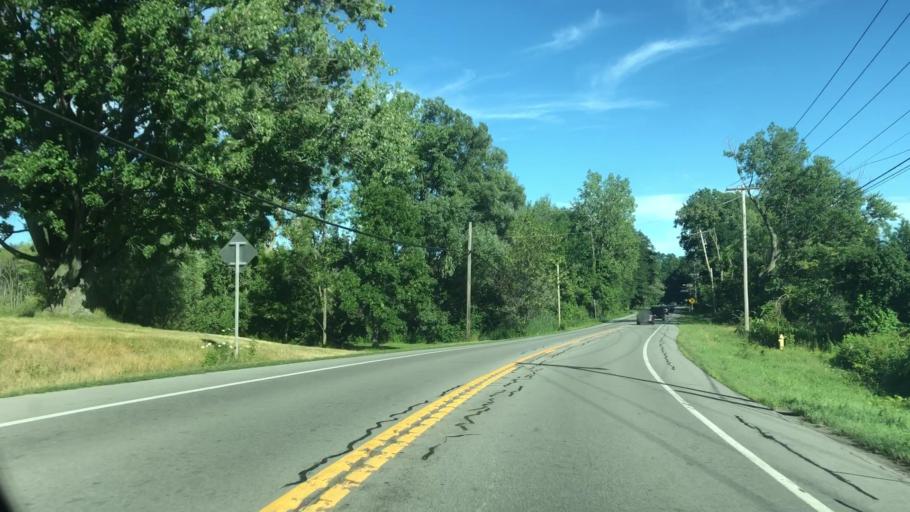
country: US
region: New York
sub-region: Monroe County
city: Fairport
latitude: 43.1303
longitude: -77.4252
